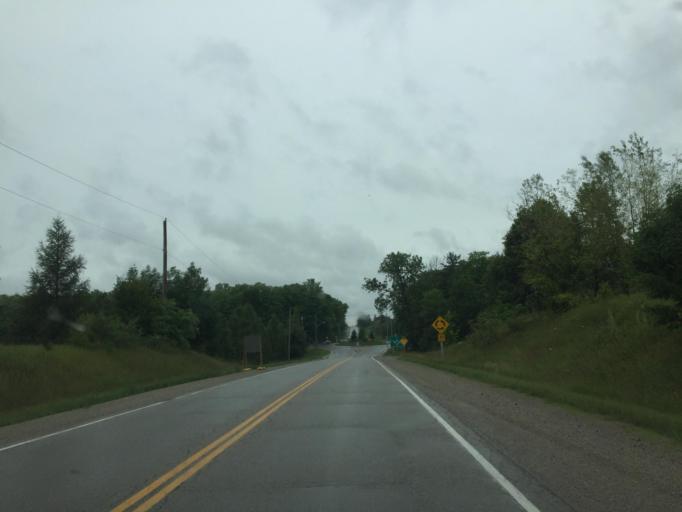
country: CA
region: Ontario
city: Cambridge
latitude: 43.4412
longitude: -80.2648
